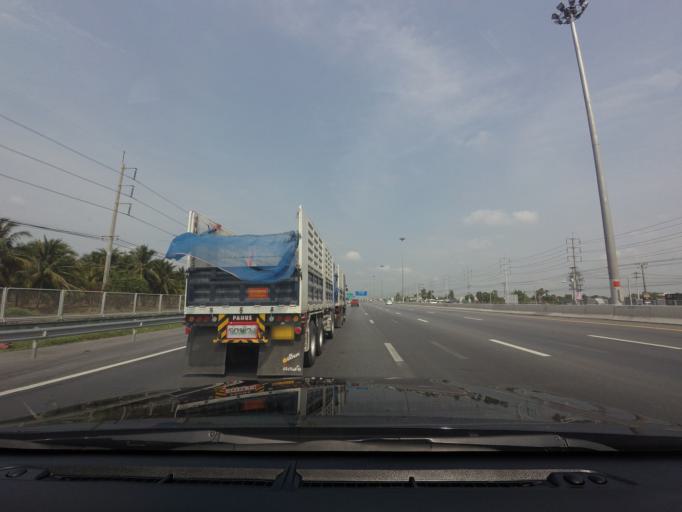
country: TH
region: Pathum Thani
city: Thanyaburi
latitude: 13.9913
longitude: 100.7122
